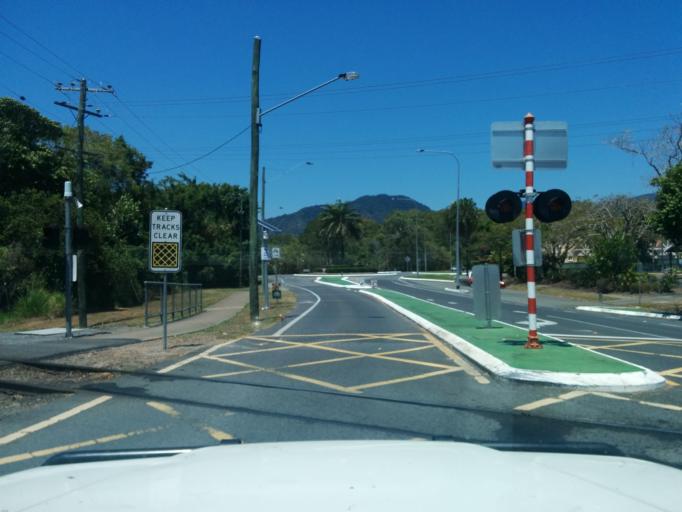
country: AU
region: Queensland
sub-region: Cairns
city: Cairns
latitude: -16.9036
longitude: 145.7560
